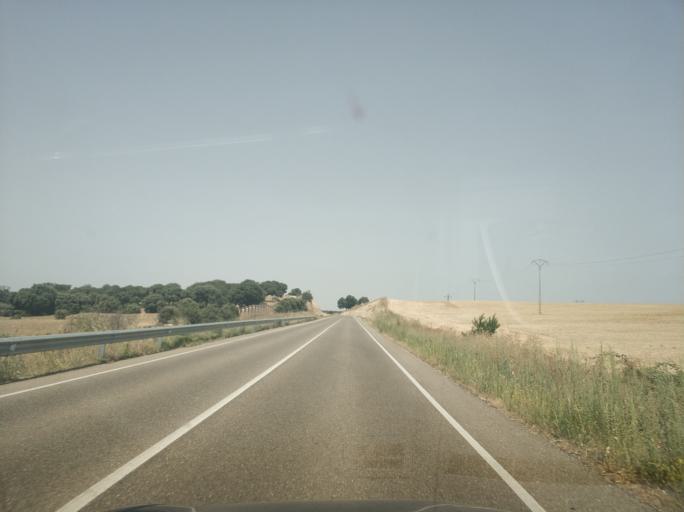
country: ES
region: Castille and Leon
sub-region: Provincia de Salamanca
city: Florida de Liebana
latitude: 41.0338
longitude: -5.7332
